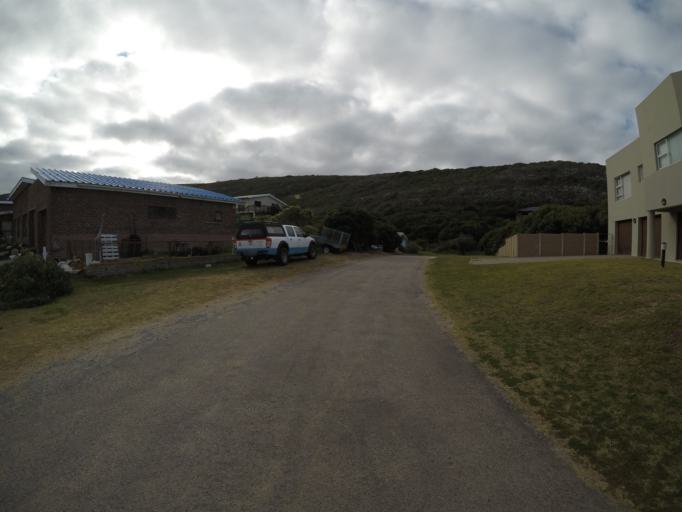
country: ZA
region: Western Cape
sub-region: Eden District Municipality
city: Riversdale
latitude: -34.4311
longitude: 21.3248
